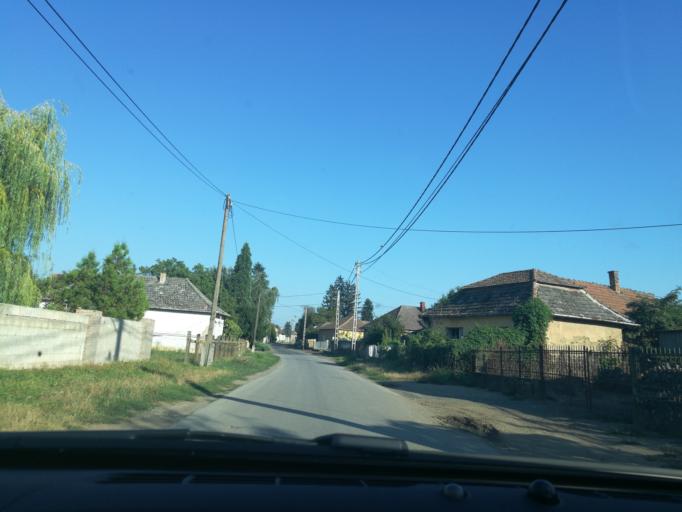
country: HU
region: Szabolcs-Szatmar-Bereg
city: Tiszabercel
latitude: 48.1670
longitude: 21.5866
